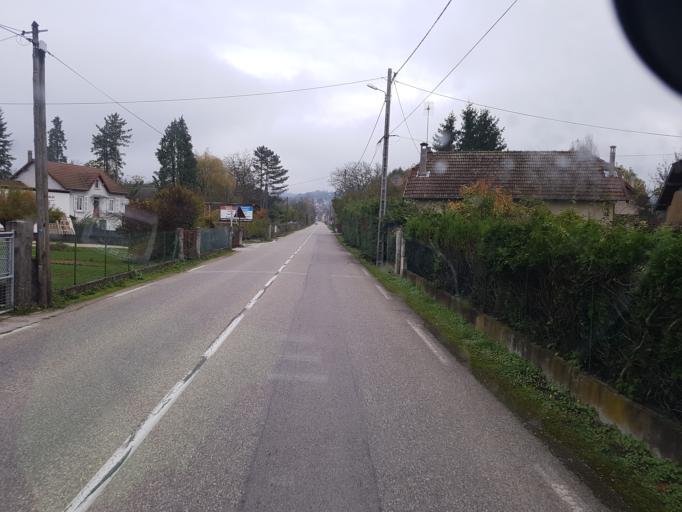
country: FR
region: Rhone-Alpes
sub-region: Departement de la Savoie
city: Saint-Genix-sur-Guiers
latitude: 45.5948
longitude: 5.6227
